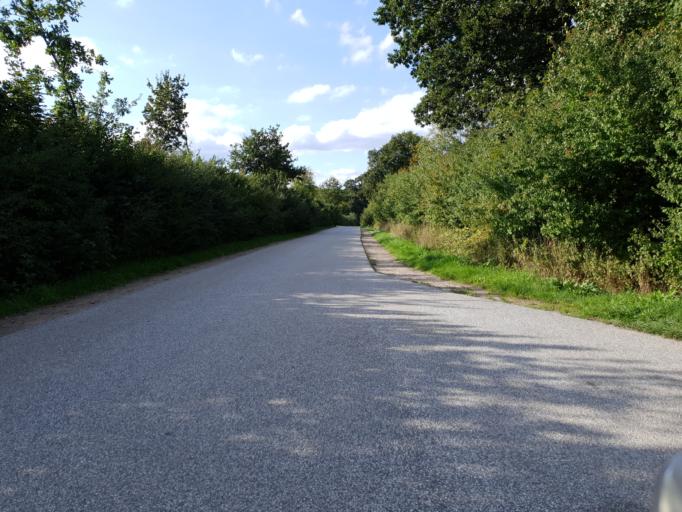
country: DE
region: Schleswig-Holstein
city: Ottendorf
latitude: 54.3519
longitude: 10.0695
